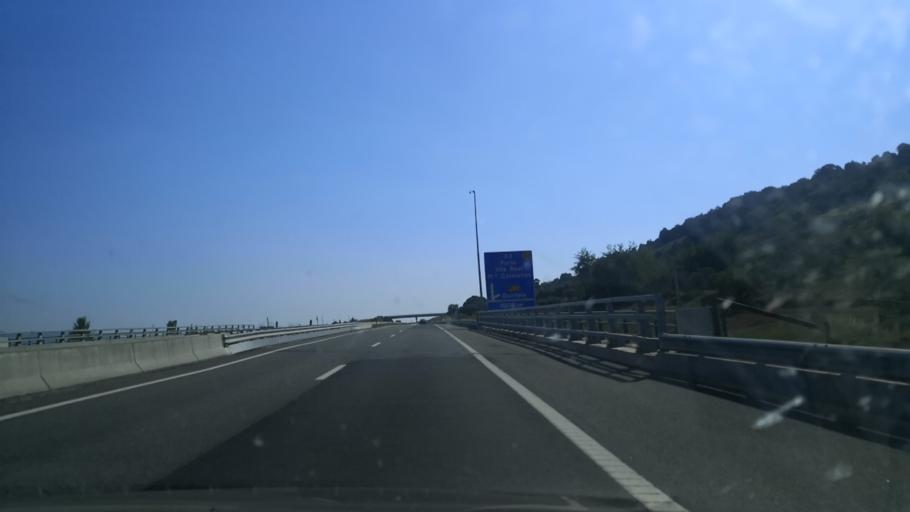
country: PT
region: Braganca
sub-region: Macedo de Cavaleiros
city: Macedo de Cavaleiros
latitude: 41.6195
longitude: -6.8689
